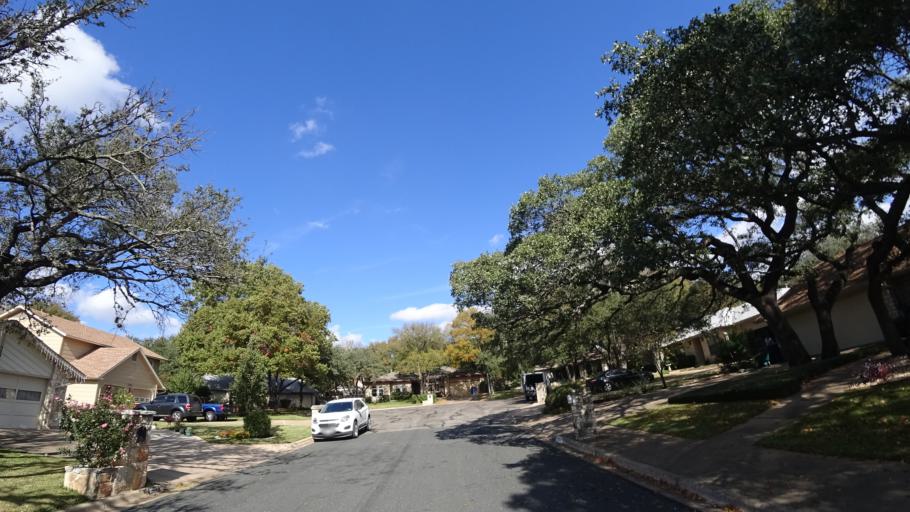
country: US
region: Texas
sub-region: Williamson County
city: Jollyville
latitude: 30.4167
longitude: -97.7267
